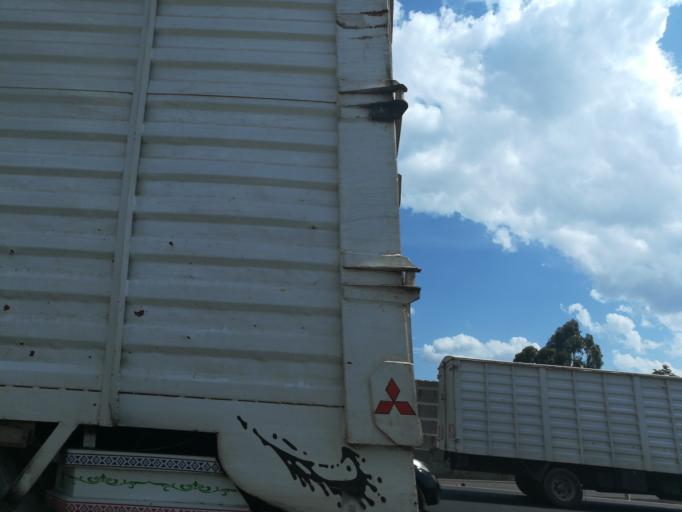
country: KE
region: Nairobi Area
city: Nairobi
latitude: -1.3312
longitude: 36.8014
